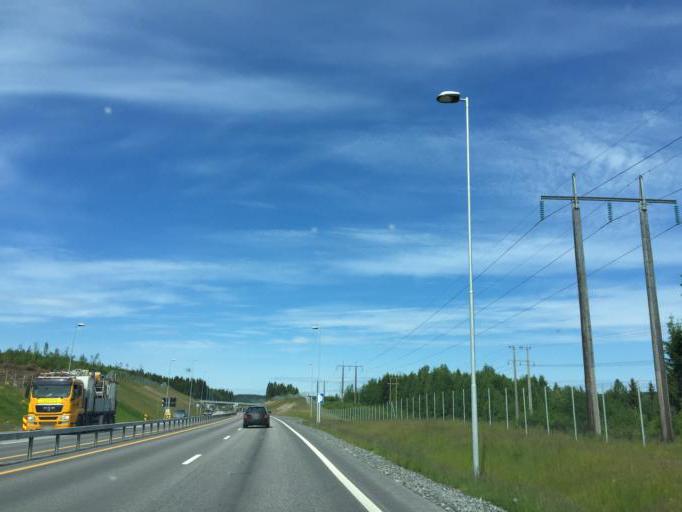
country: NO
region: Hedmark
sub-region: Kongsvinger
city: Kongsvinger
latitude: 60.1976
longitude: 11.9700
